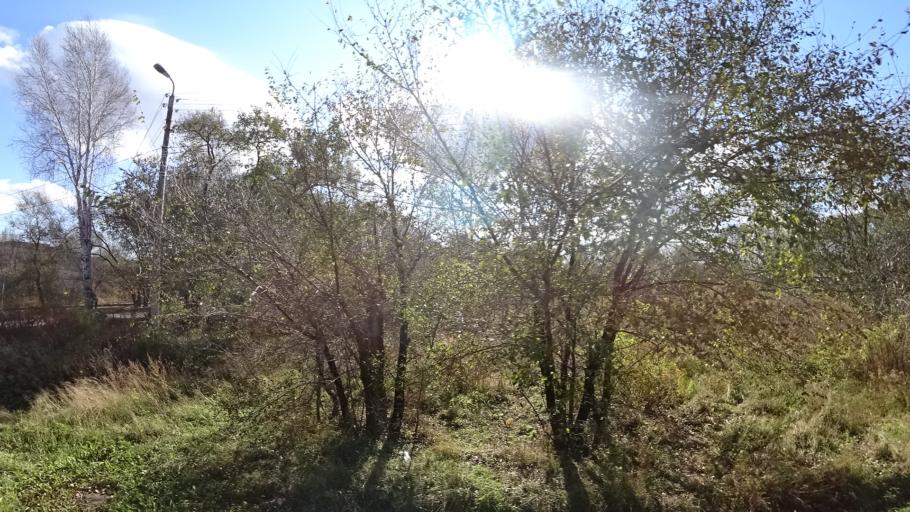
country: RU
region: Khabarovsk Krai
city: Amursk
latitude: 50.0982
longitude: 136.4972
